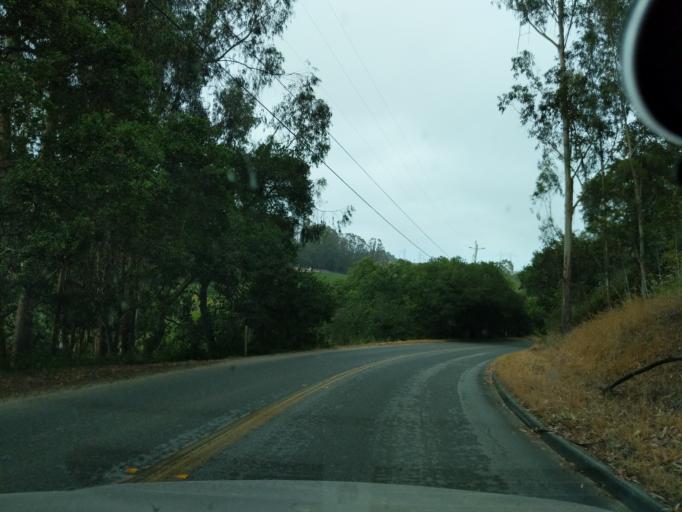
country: US
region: California
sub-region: Monterey County
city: Elkhorn
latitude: 36.8140
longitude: -121.7232
